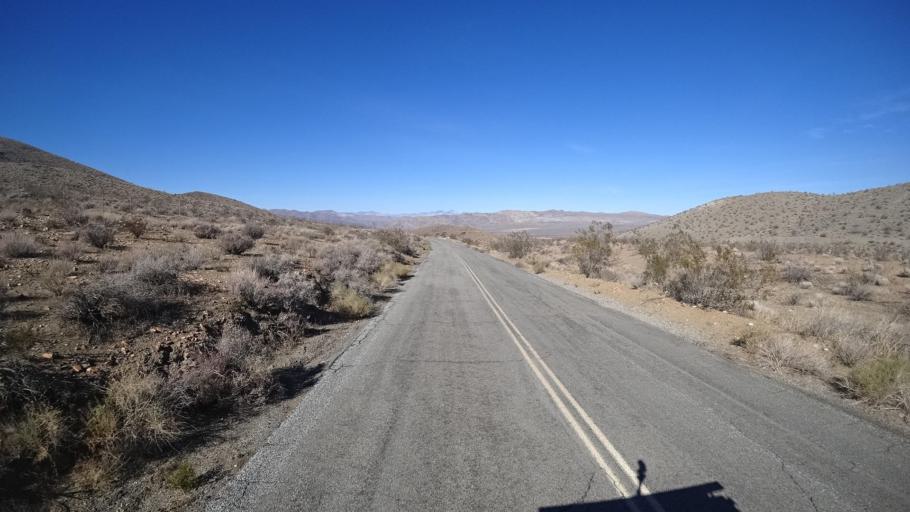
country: US
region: California
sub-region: Kern County
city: Ridgecrest
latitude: 35.3747
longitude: -117.6619
